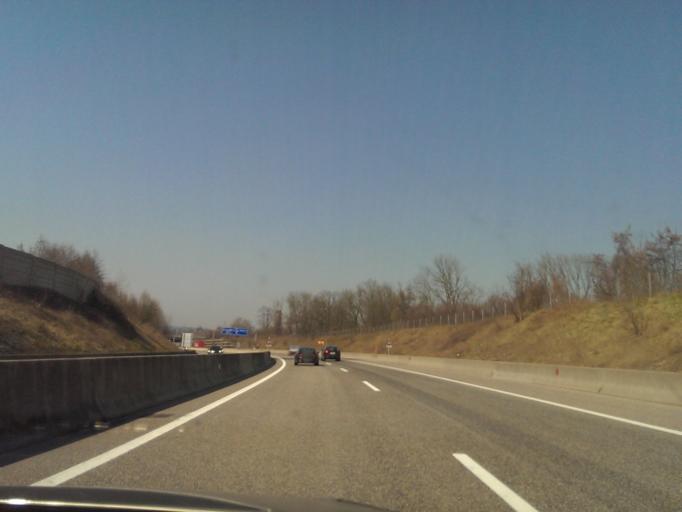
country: AT
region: Upper Austria
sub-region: Wels-Land
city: Steinhaus
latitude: 48.1359
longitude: 14.0016
